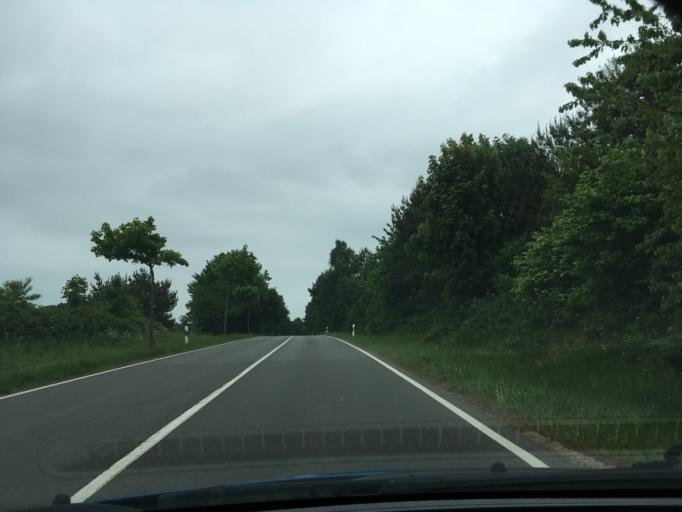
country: DE
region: Lower Saxony
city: Buchholz in der Nordheide
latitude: 53.3478
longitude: 9.8735
